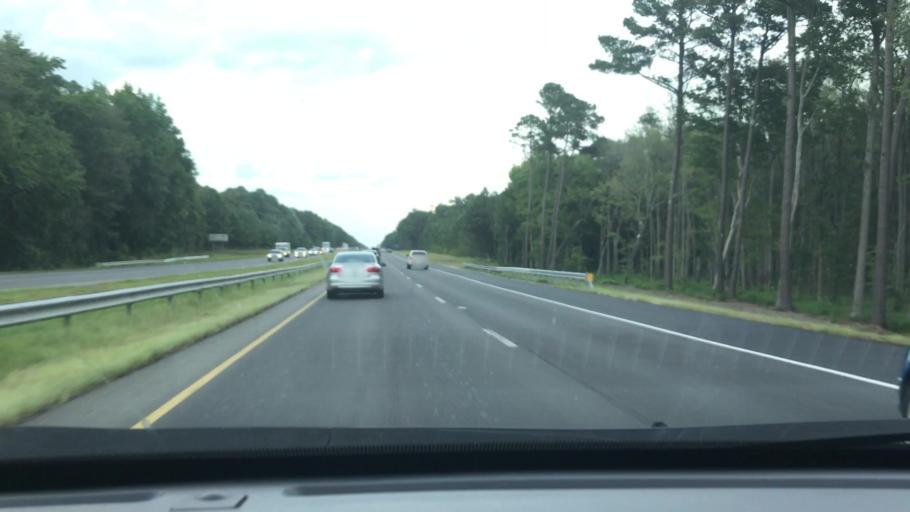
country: US
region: North Carolina
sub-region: Cumberland County
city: Eastover
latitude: 35.1432
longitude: -78.7329
